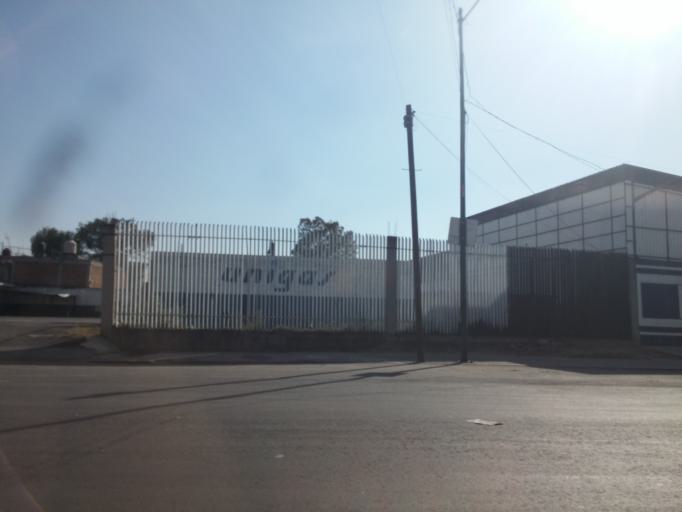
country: MX
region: Mexico City
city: Azcapotzalco
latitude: 19.4903
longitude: -99.1670
